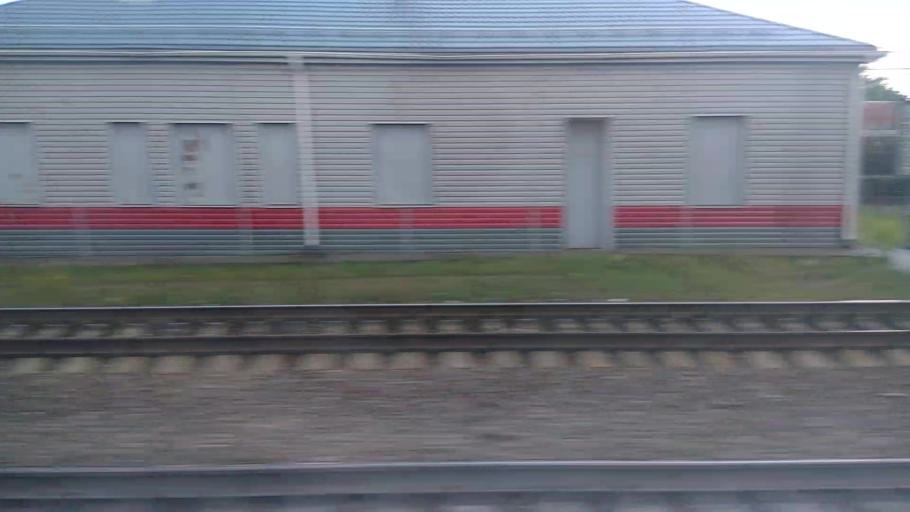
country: RU
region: Moskovskaya
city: Mikhnevo
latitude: 55.1242
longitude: 37.9600
